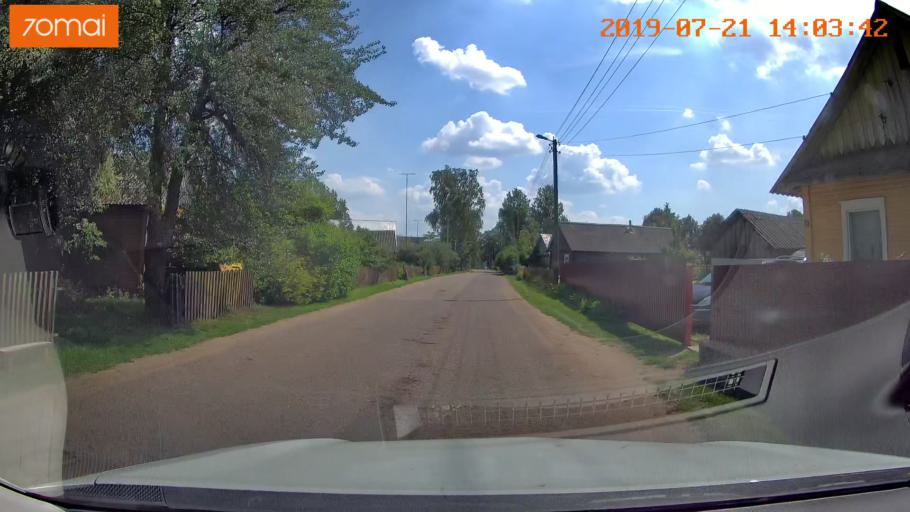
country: BY
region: Grodnenskaya
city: Lyubcha
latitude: 53.7270
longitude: 26.0931
